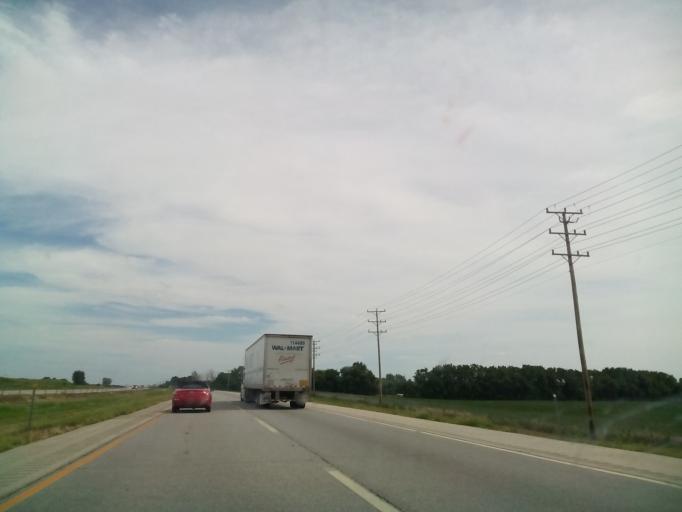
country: US
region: Illinois
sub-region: Kane County
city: Sugar Grove
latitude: 41.8023
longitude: -88.4264
